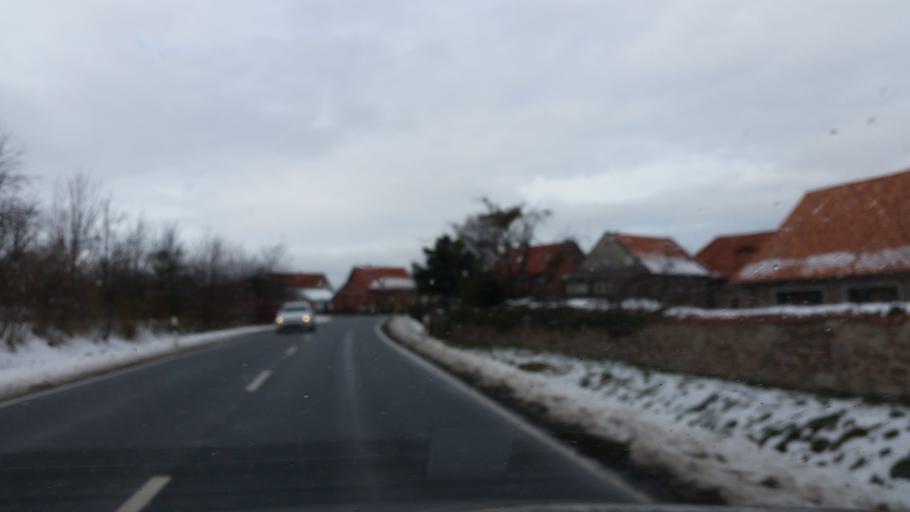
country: DE
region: Saxony-Anhalt
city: Drubeck
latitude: 51.8554
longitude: 10.7139
